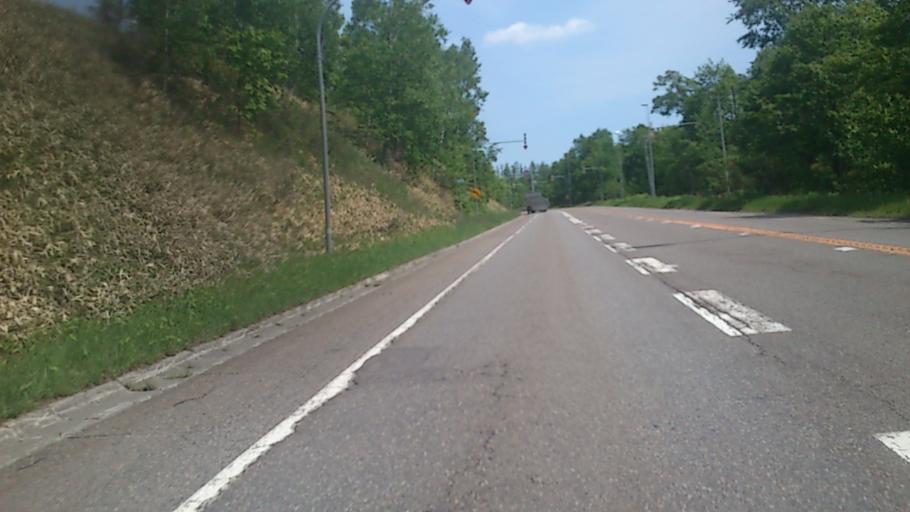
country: JP
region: Hokkaido
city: Otofuke
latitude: 43.2329
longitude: 143.4963
